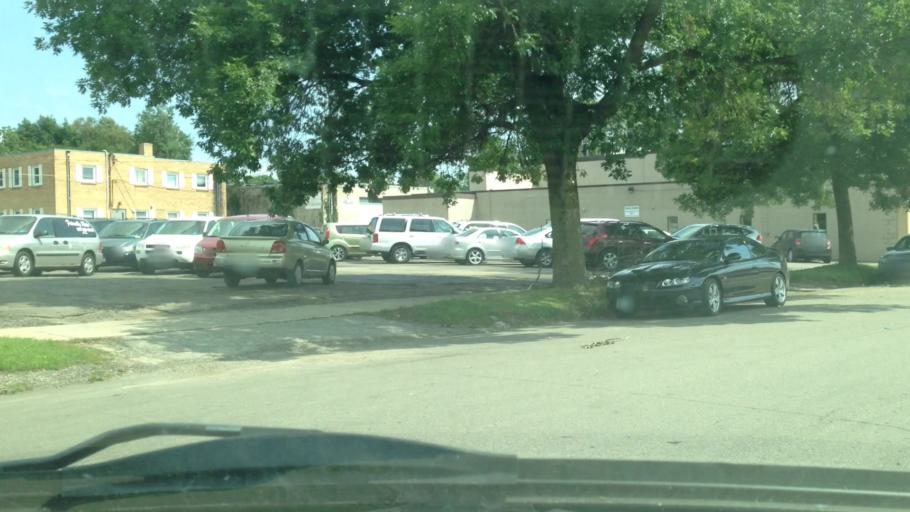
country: US
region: Minnesota
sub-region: Olmsted County
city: Rochester
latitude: 44.0388
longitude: -92.4607
